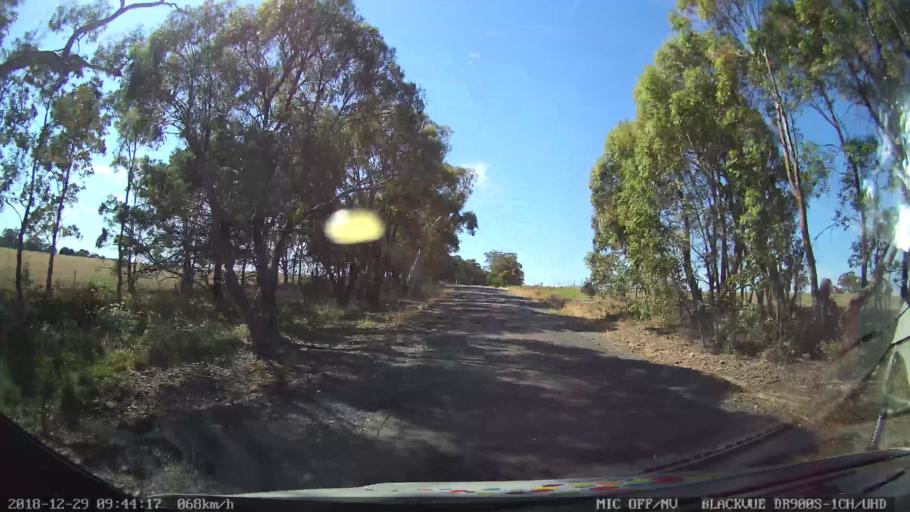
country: AU
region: New South Wales
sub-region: Upper Lachlan Shire
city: Crookwell
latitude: -34.6877
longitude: 149.4257
